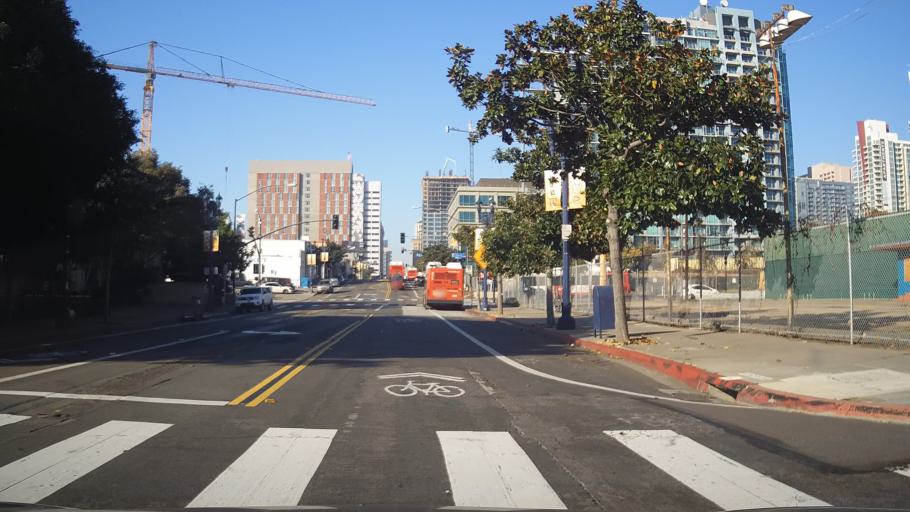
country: US
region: California
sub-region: San Diego County
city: San Diego
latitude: 32.7158
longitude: -117.1520
